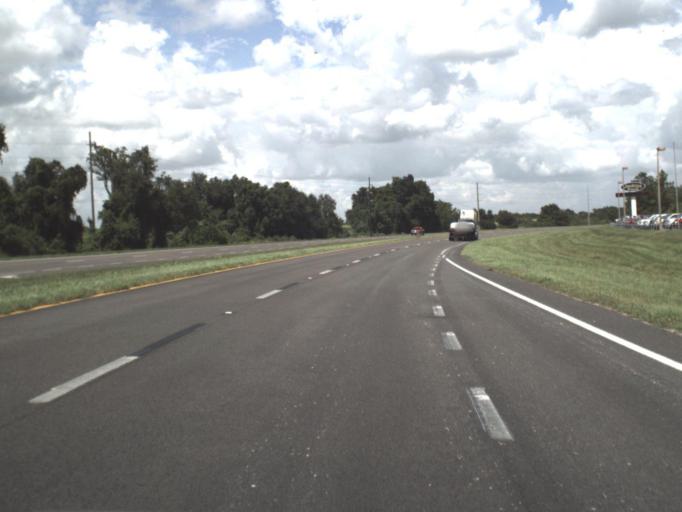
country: US
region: Florida
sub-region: Polk County
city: Fort Meade
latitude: 27.7882
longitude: -81.8124
